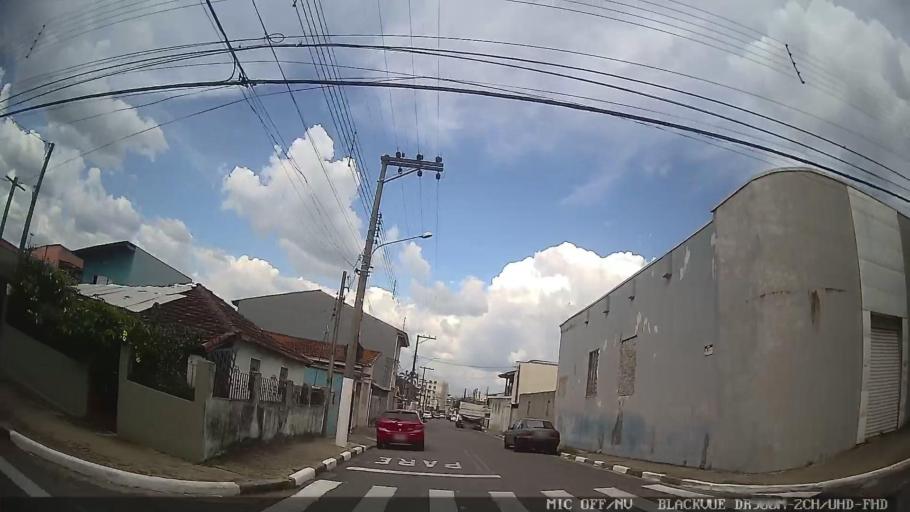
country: BR
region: Sao Paulo
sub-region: Atibaia
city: Atibaia
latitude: -23.1192
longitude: -46.5683
